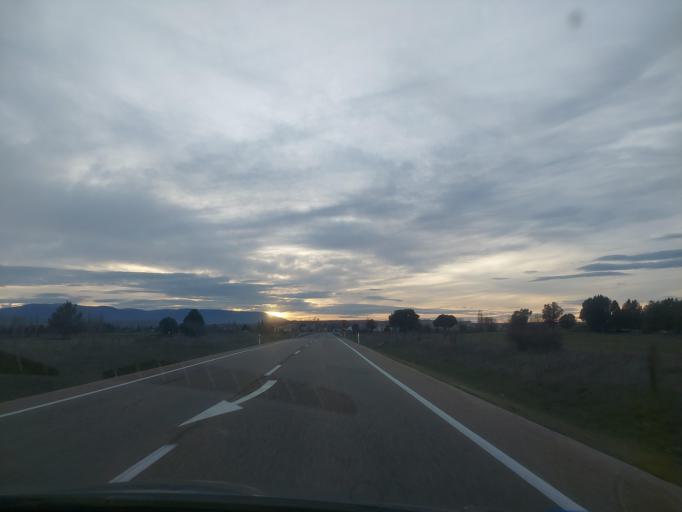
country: ES
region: Castille and Leon
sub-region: Provincia de Segovia
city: Arcones
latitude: 41.1199
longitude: -3.7156
